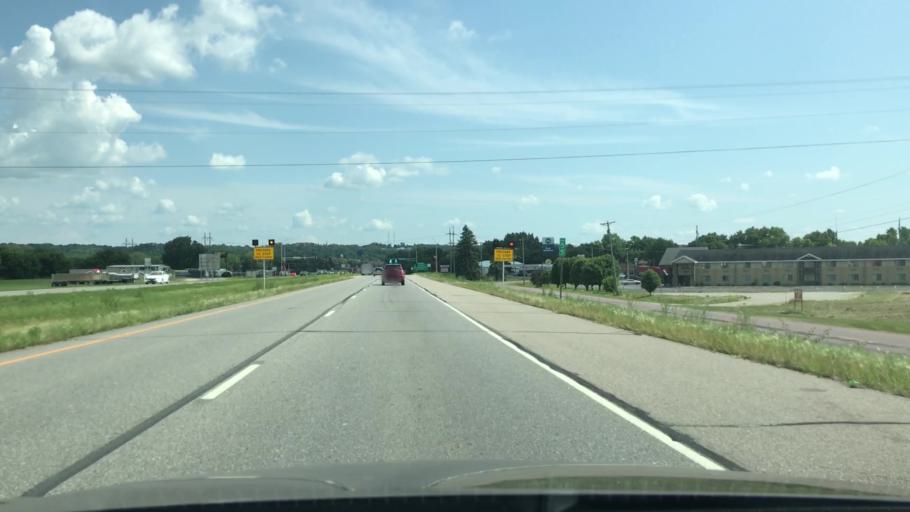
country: US
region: Minnesota
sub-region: Blue Earth County
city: Mankato
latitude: 44.1836
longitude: -94.0100
